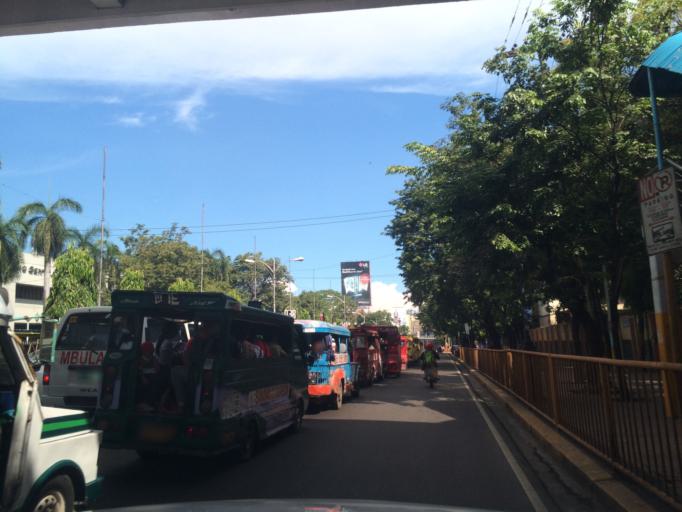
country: PH
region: Central Visayas
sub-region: Cebu City
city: Calero
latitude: 10.3010
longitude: 123.8962
